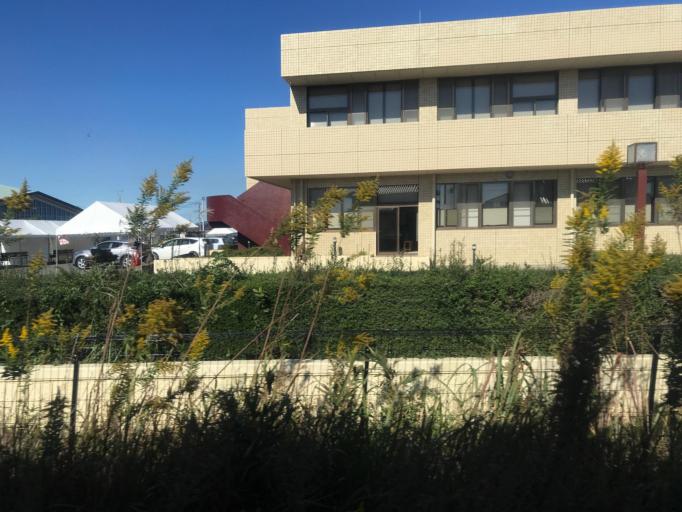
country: JP
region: Chiba
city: Omigawa
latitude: 35.8368
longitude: 140.6676
